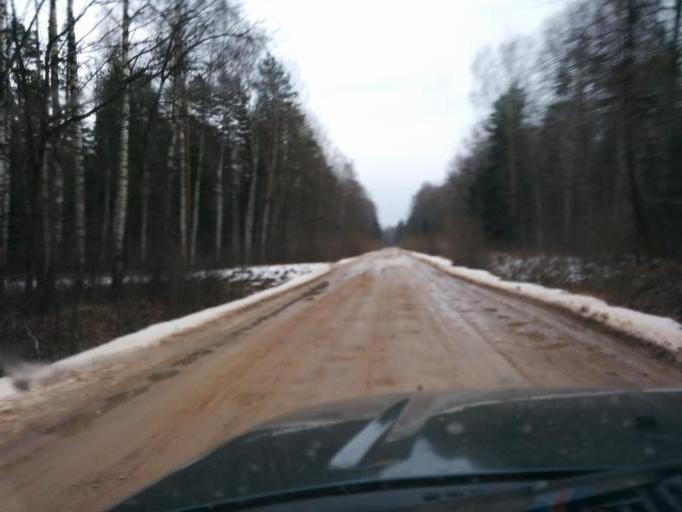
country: LV
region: Ozolnieku
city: Ozolnieki
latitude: 56.6849
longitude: 23.7716
